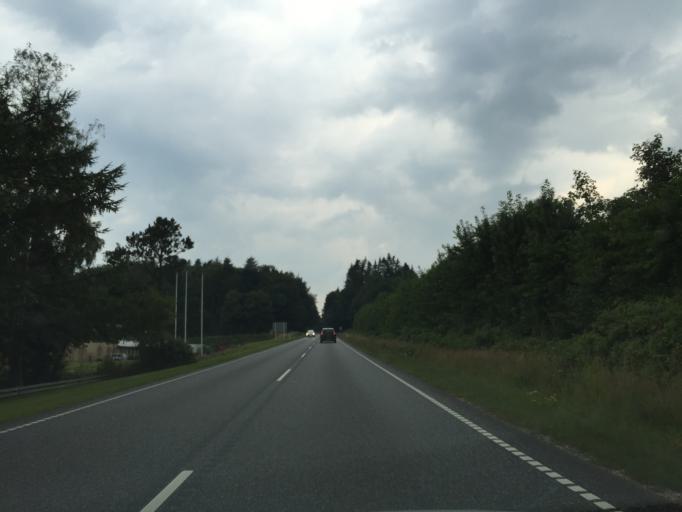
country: DK
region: Central Jutland
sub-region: Viborg Kommune
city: Bjerringbro
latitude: 56.3119
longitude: 9.5826
